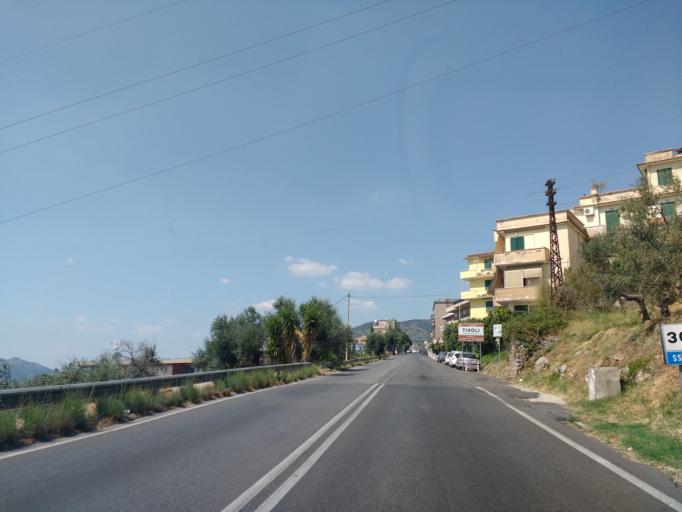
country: IT
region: Latium
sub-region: Citta metropolitana di Roma Capitale
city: Tivoli
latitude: 41.9523
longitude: 12.7911
